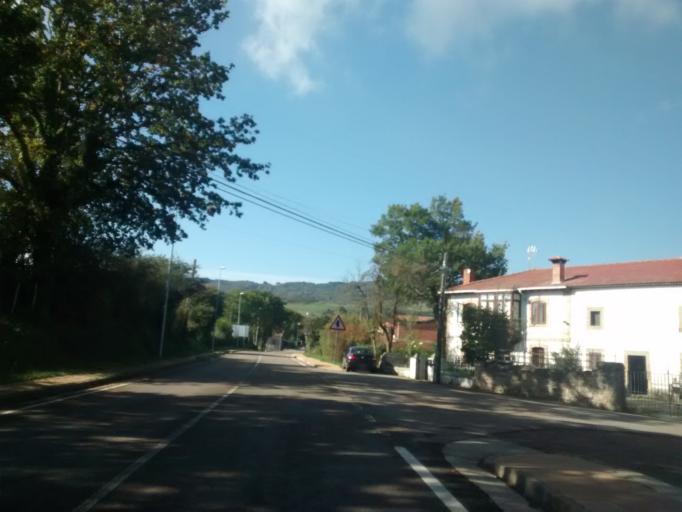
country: ES
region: Cantabria
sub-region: Provincia de Cantabria
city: Reinosa
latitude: 42.9706
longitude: -4.0588
